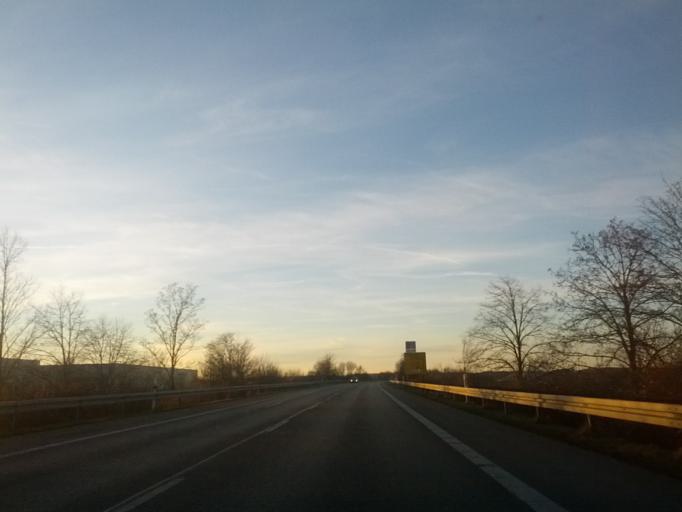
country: DE
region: Bavaria
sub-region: Swabia
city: Heimertingen
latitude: 48.0353
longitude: 10.1251
